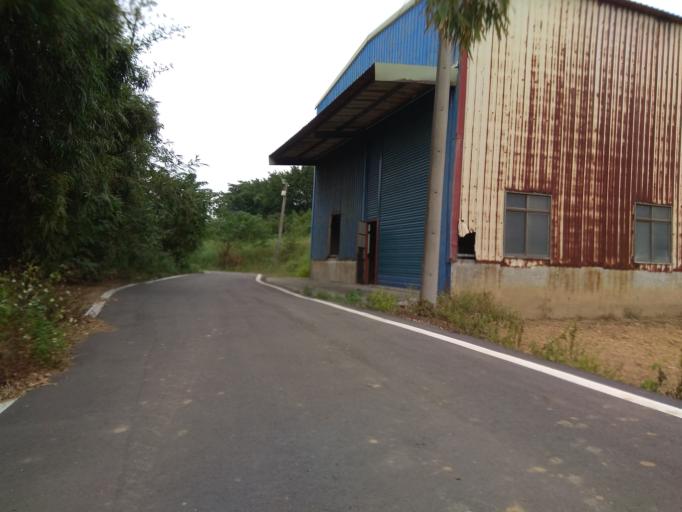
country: TW
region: Taiwan
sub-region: Hsinchu
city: Zhubei
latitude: 24.9758
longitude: 121.0423
